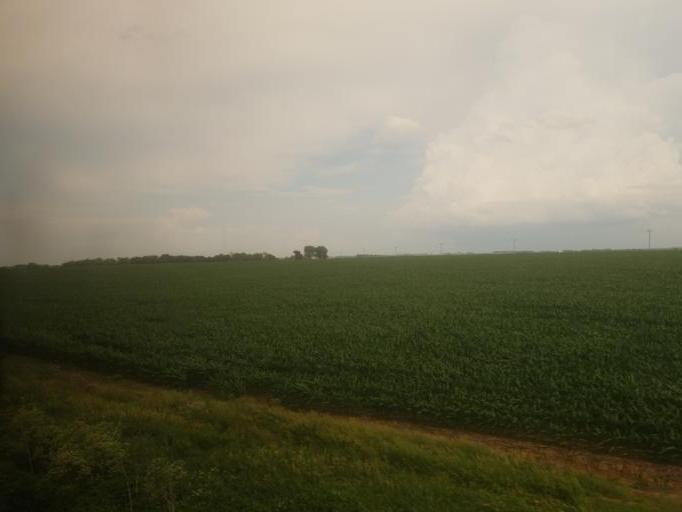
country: US
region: Illinois
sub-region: Henry County
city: Galva
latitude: 41.1370
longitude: -90.1094
